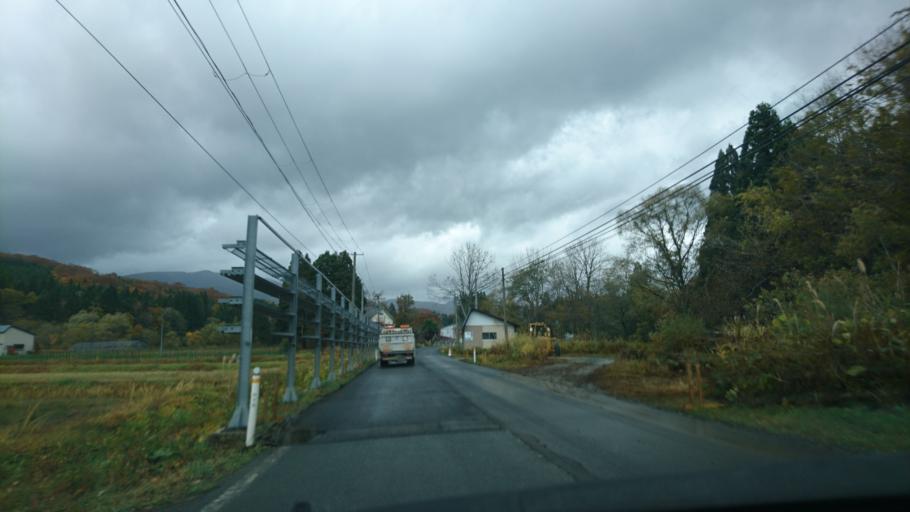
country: JP
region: Iwate
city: Shizukuishi
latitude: 39.5212
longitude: 140.8280
